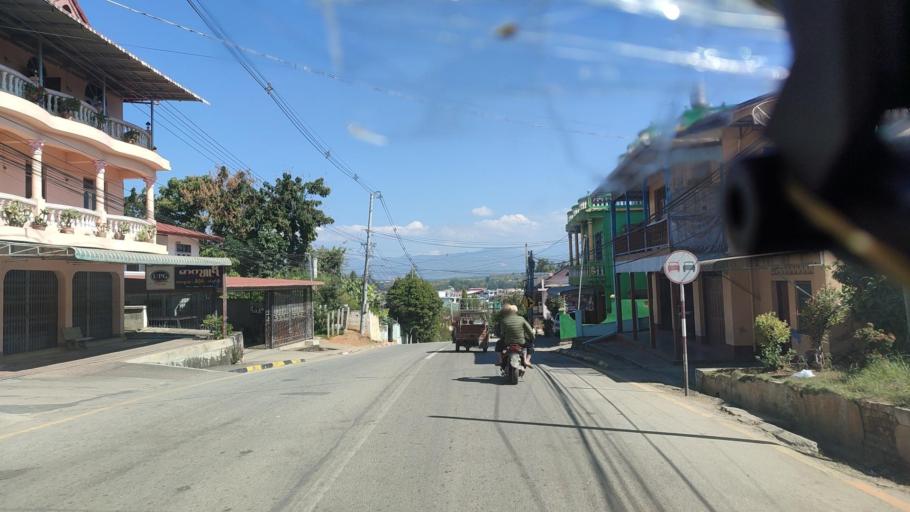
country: TH
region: Chiang Rai
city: Mae Sai
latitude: 21.2954
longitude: 99.6085
